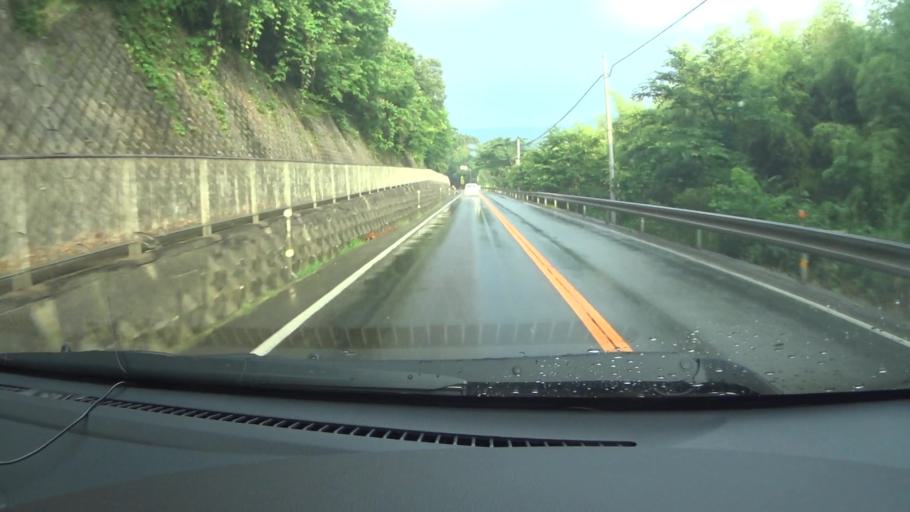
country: JP
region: Kyoto
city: Ayabe
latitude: 35.2886
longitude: 135.2851
